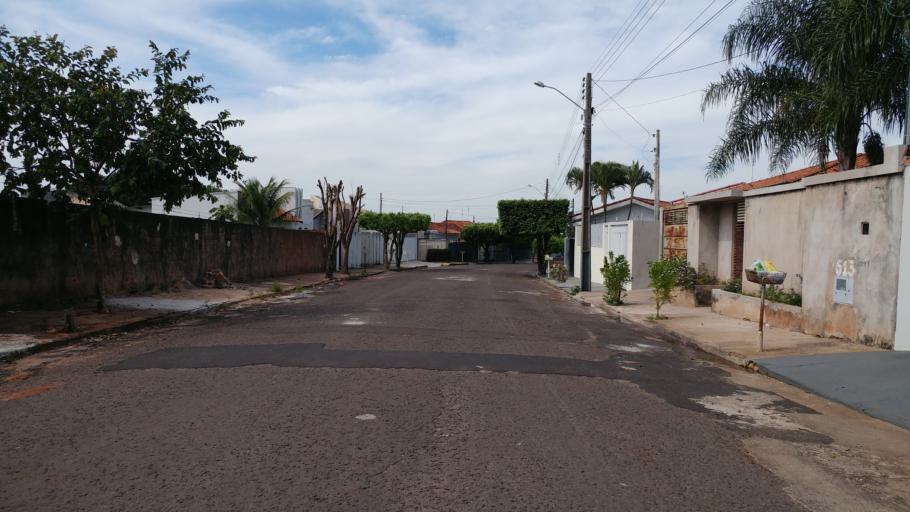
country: BR
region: Sao Paulo
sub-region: Paraguacu Paulista
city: Paraguacu Paulista
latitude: -22.4058
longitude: -50.5804
